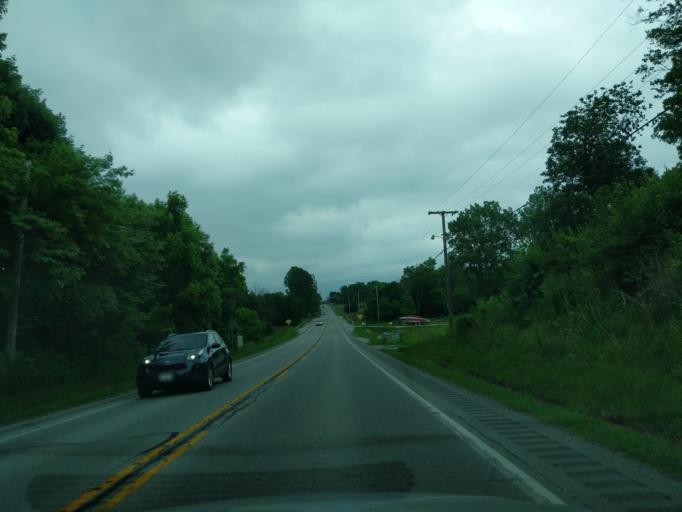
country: US
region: Indiana
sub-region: Madison County
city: Alexandria
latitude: 40.2773
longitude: -85.6927
